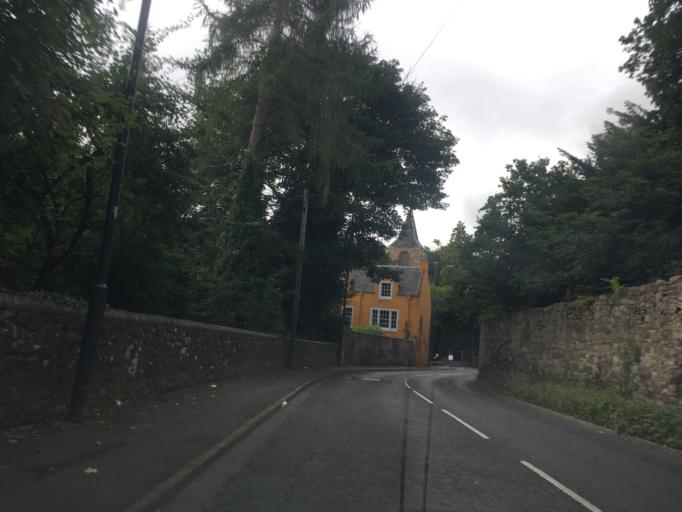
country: GB
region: Scotland
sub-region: Midlothian
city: Dalkeith
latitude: 55.8822
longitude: -3.0710
